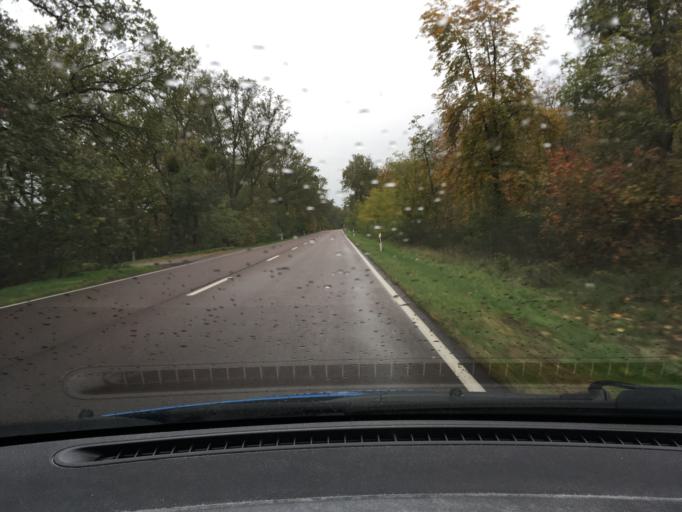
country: DE
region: Saxony-Anhalt
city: Vockerode
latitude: 51.8863
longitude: 12.3053
